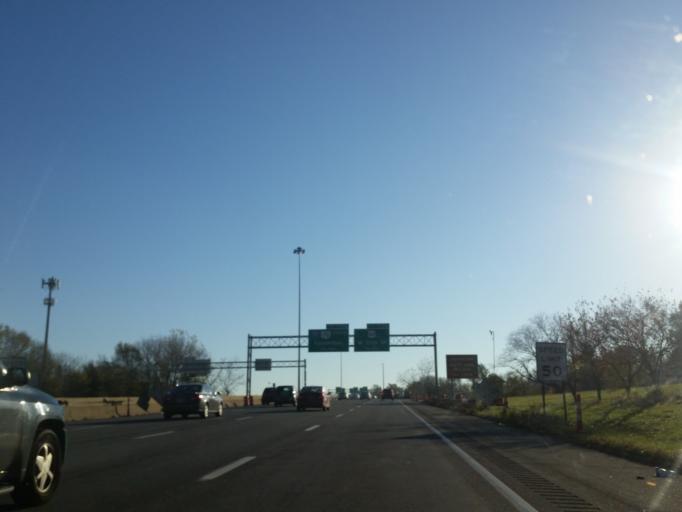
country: US
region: Ohio
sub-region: Cuyahoga County
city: Cleveland
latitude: 41.4747
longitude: -81.7133
